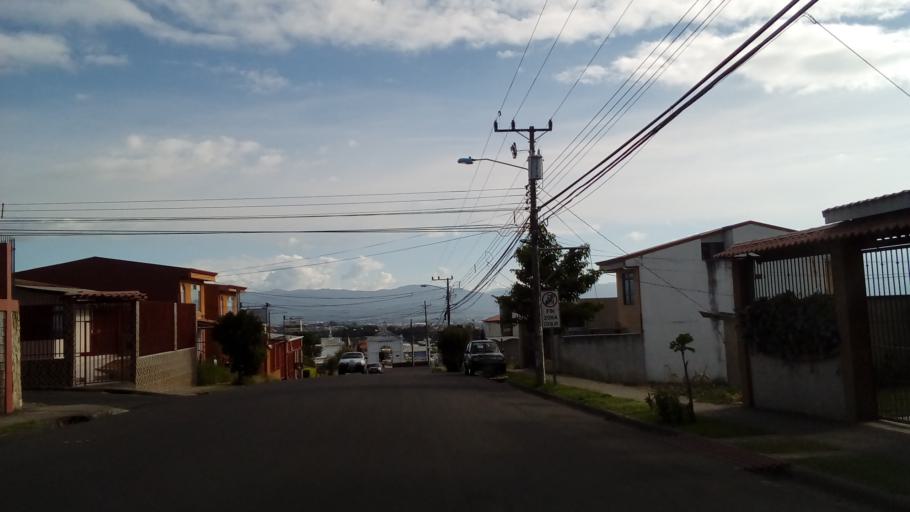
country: CR
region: Heredia
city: Angeles
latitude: 10.0123
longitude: -84.0543
